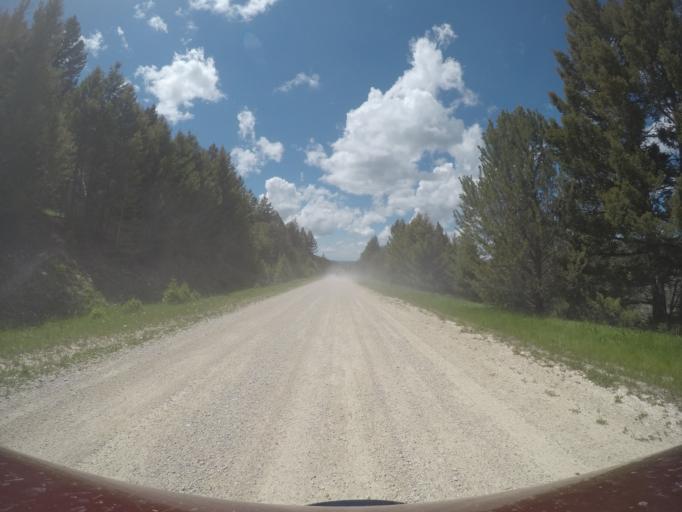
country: US
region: Wyoming
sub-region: Big Horn County
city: Lovell
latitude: 45.2042
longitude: -108.5233
